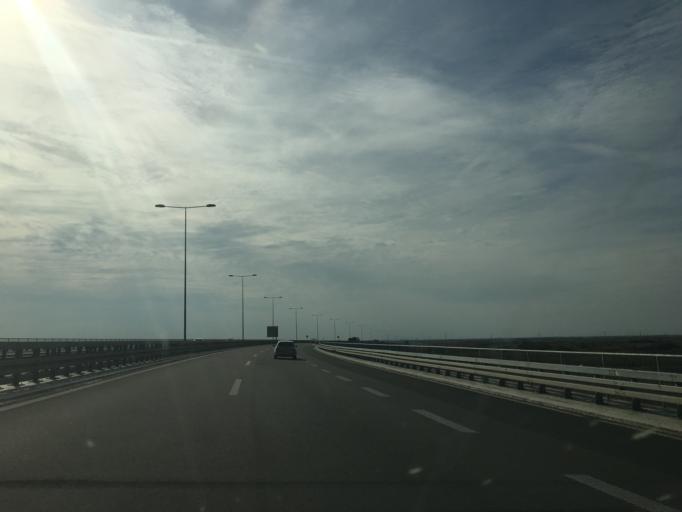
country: RS
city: Novi Banovci
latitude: 44.8898
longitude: 20.2946
